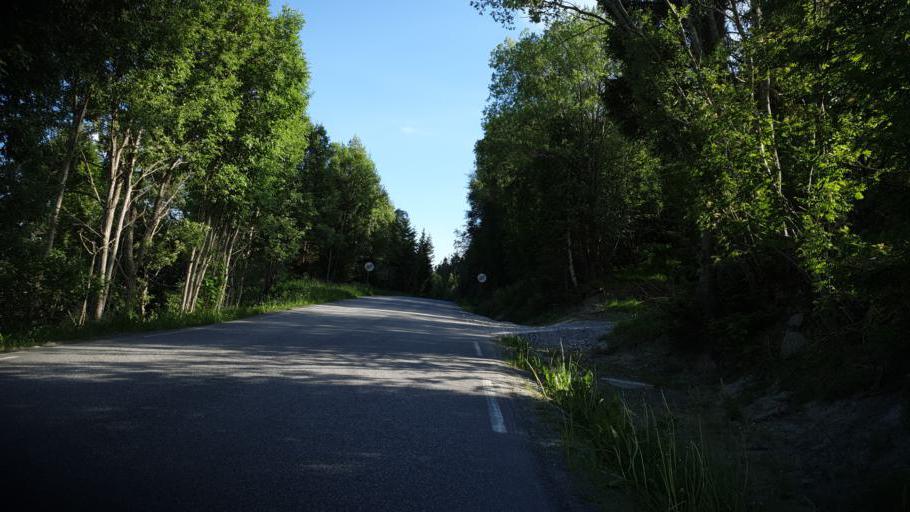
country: NO
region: Sor-Trondelag
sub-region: Trondheim
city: Trondheim
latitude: 63.5797
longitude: 10.4166
